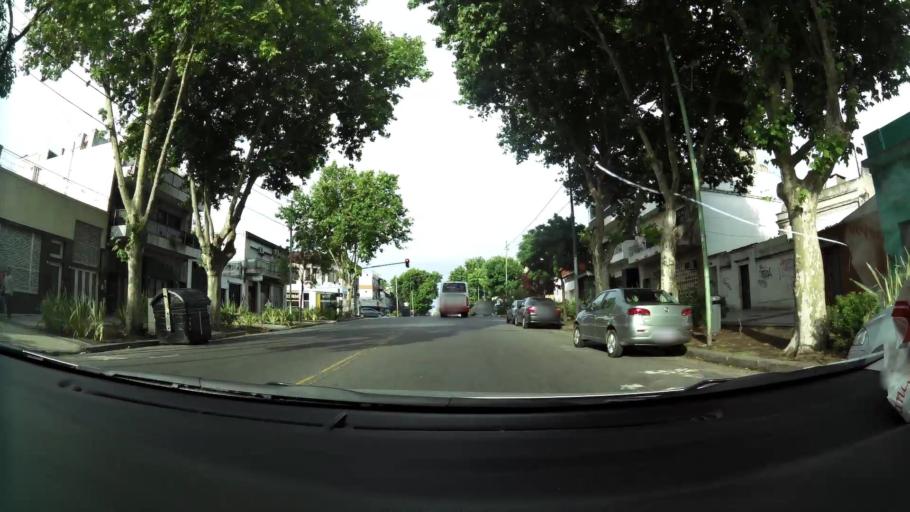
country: AR
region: Buenos Aires F.D.
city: Villa Santa Rita
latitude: -34.6419
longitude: -58.4586
